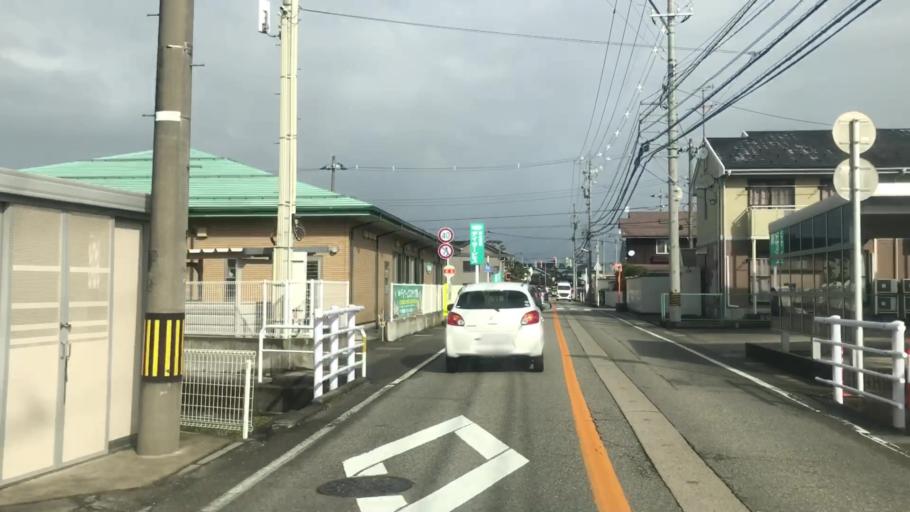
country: JP
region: Toyama
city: Toyama-shi
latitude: 36.6541
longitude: 137.2175
